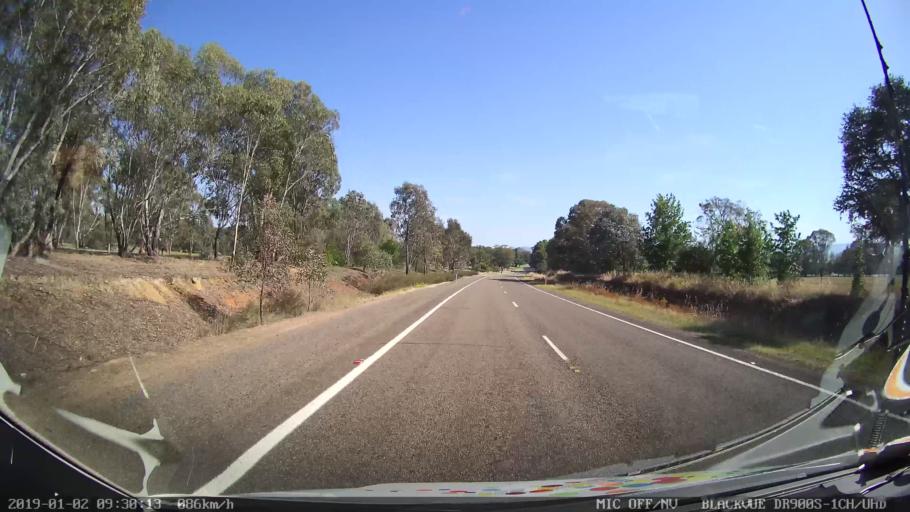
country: AU
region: New South Wales
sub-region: Tumut Shire
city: Tumut
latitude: -35.3292
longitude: 148.2376
